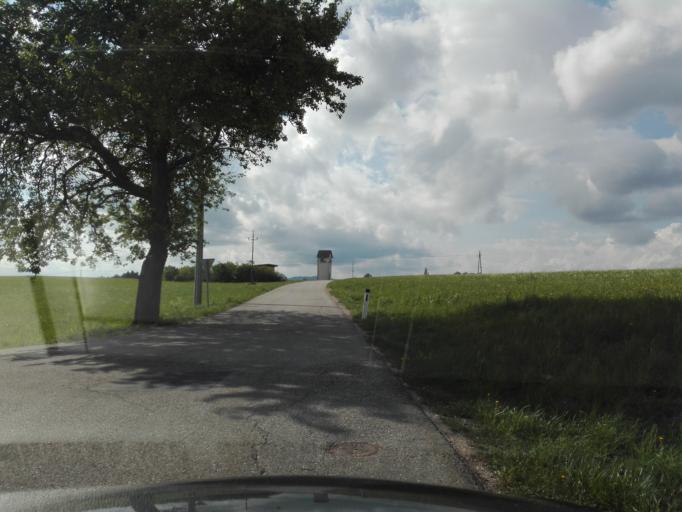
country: AT
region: Upper Austria
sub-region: Politischer Bezirk Rohrbach
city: Pfarrkirchen im Muehlkreis
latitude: 48.4462
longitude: 13.8055
